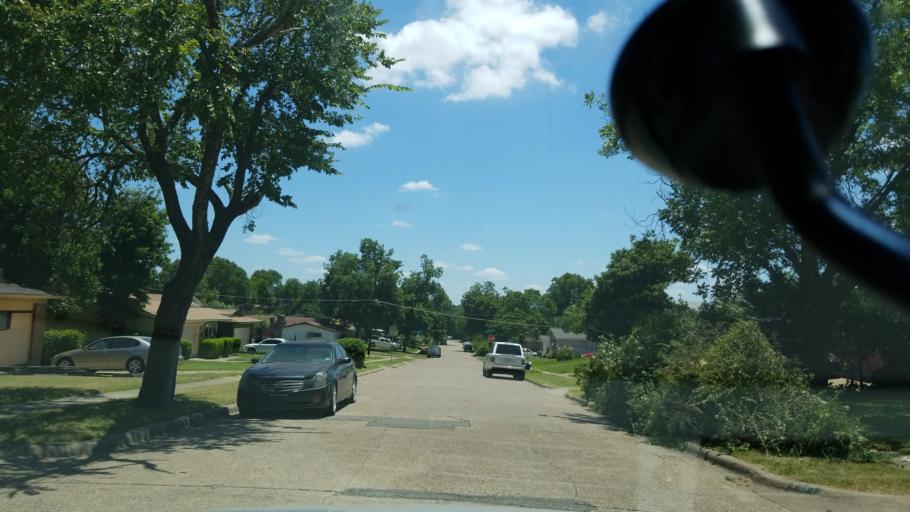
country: US
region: Texas
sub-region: Dallas County
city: Cockrell Hill
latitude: 32.6968
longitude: -96.8179
